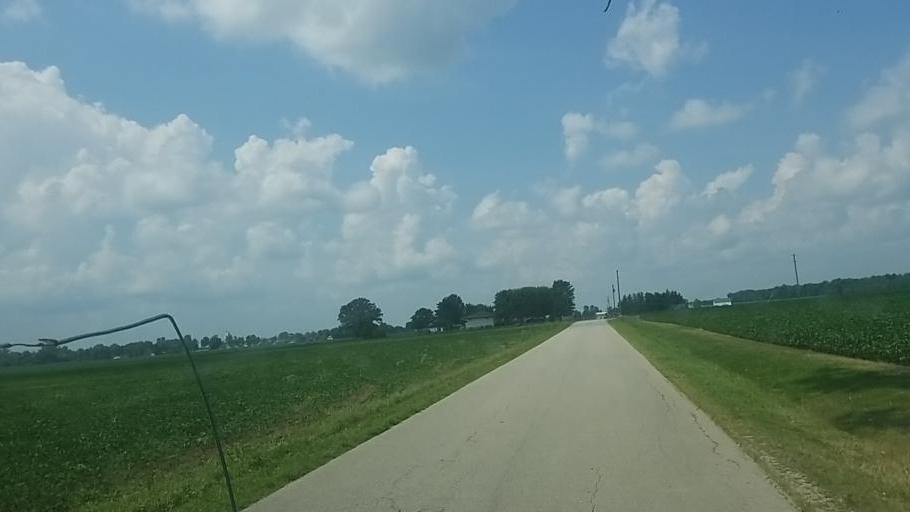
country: US
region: Ohio
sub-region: Crawford County
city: Galion
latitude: 40.7993
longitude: -82.8436
